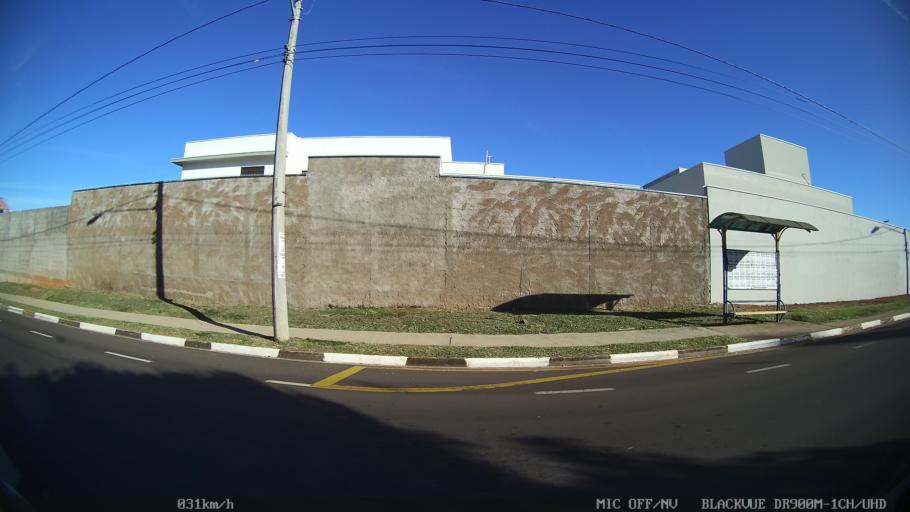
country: BR
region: Sao Paulo
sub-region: Franca
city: Franca
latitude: -20.5666
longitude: -47.3654
